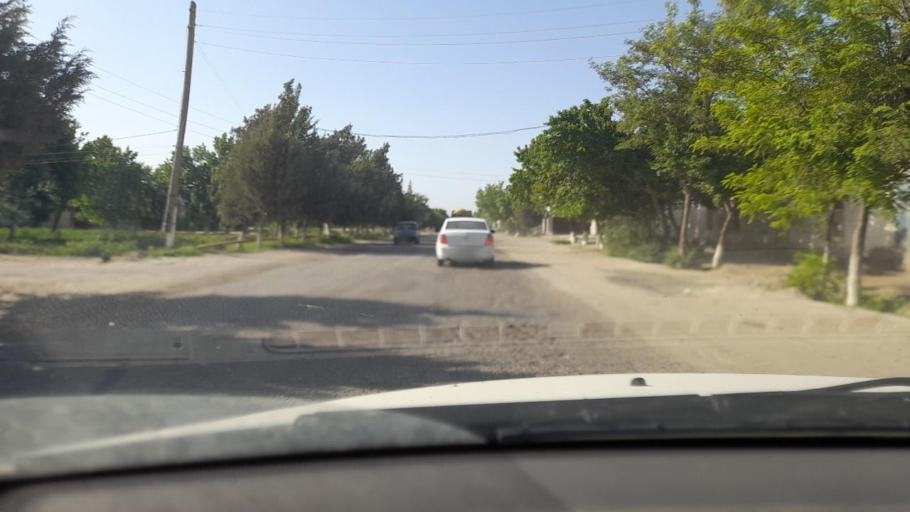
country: UZ
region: Bukhara
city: Romiton
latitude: 40.0621
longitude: 64.3274
